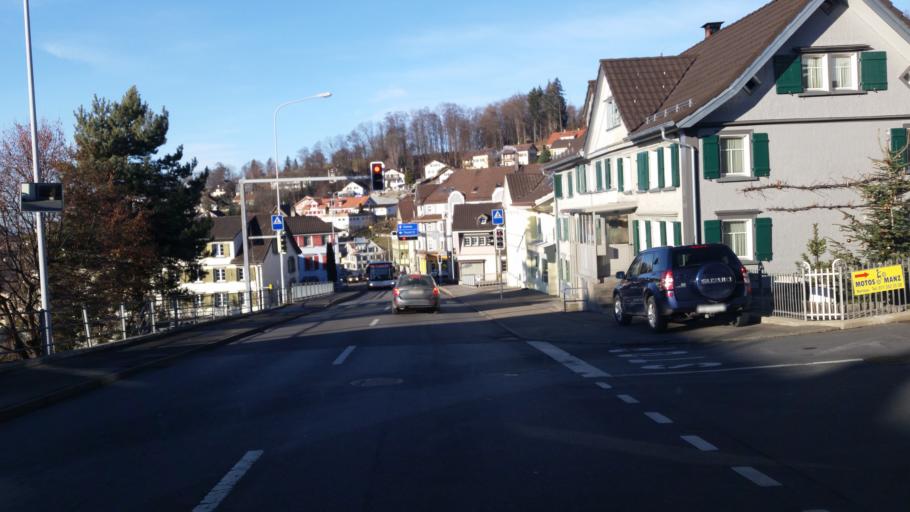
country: CH
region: Appenzell Ausserrhoden
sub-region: Bezirk Hinterland
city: Herisau
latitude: 47.3906
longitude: 9.2729
